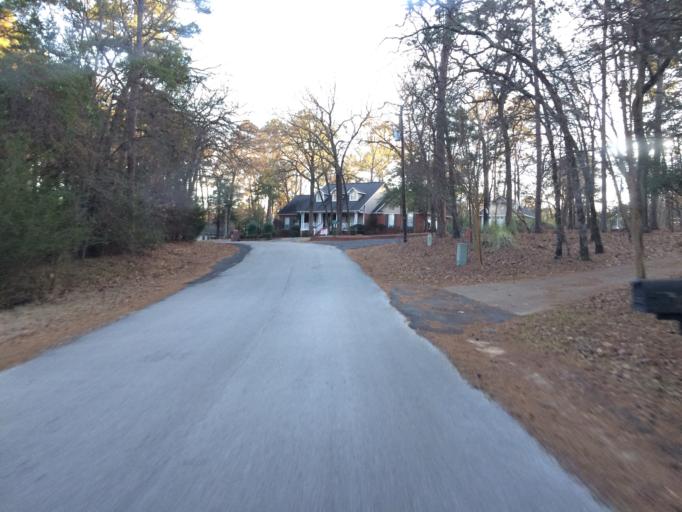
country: US
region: Texas
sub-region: Wood County
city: Hawkins
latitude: 32.7262
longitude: -95.1878
